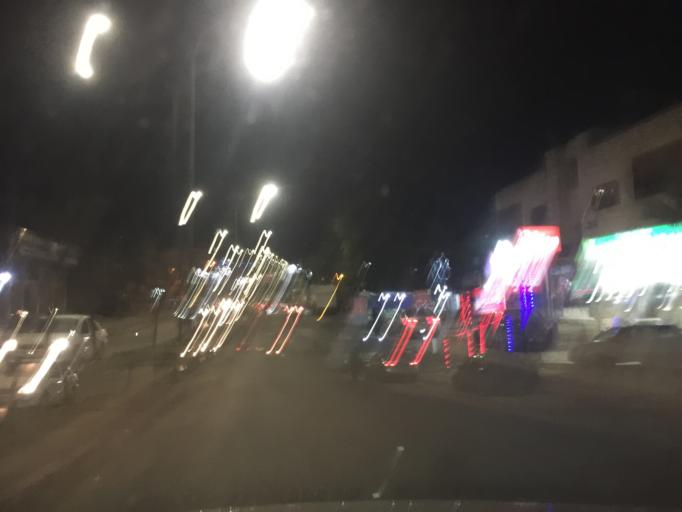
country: JO
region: Zarqa
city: Russeifa
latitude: 32.0282
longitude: 36.0324
